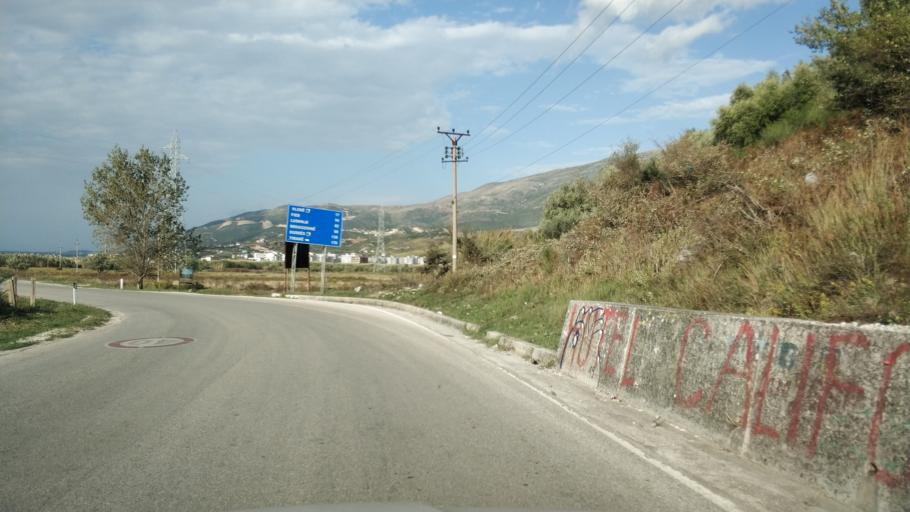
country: AL
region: Vlore
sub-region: Rrethi i Vlores
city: Orikum
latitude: 40.3325
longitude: 19.4779
